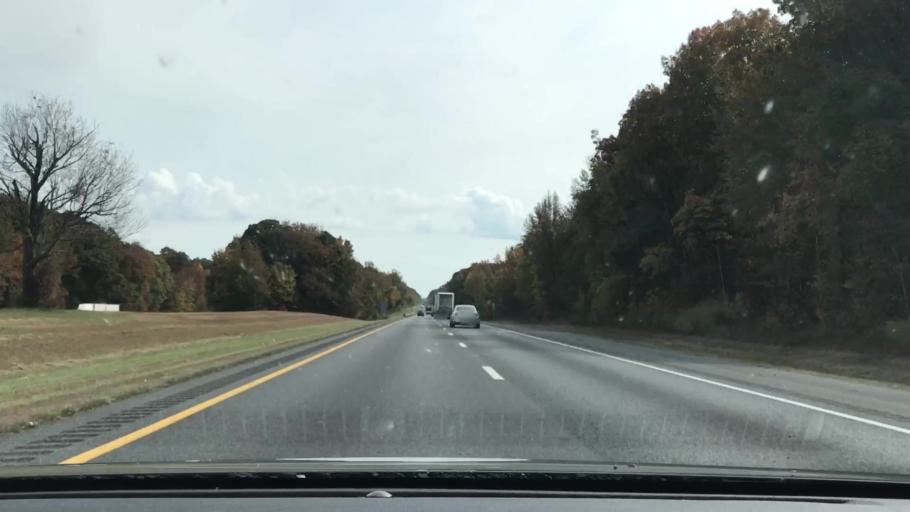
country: US
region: Kentucky
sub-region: Todd County
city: Guthrie
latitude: 36.5040
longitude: -87.1903
